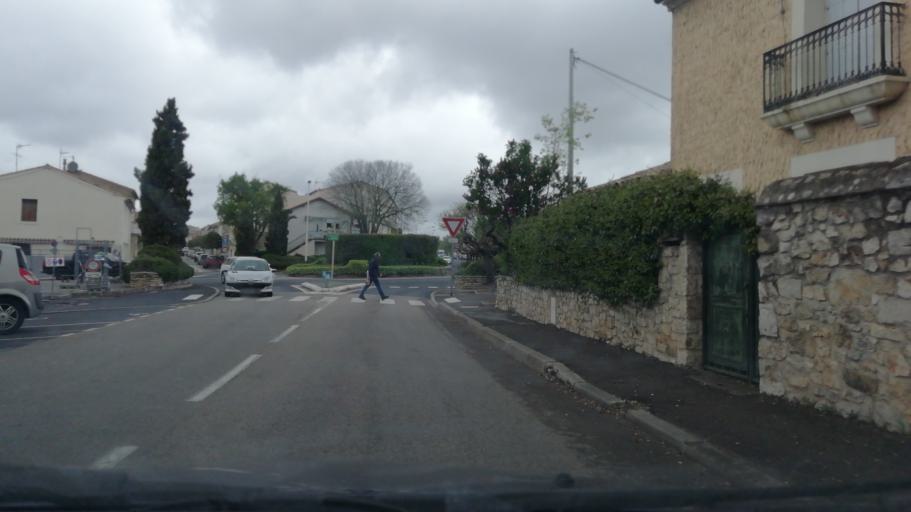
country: FR
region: Languedoc-Roussillon
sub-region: Departement de l'Herault
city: Saint-Gely-du-Fesc
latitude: 43.6902
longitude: 3.8074
